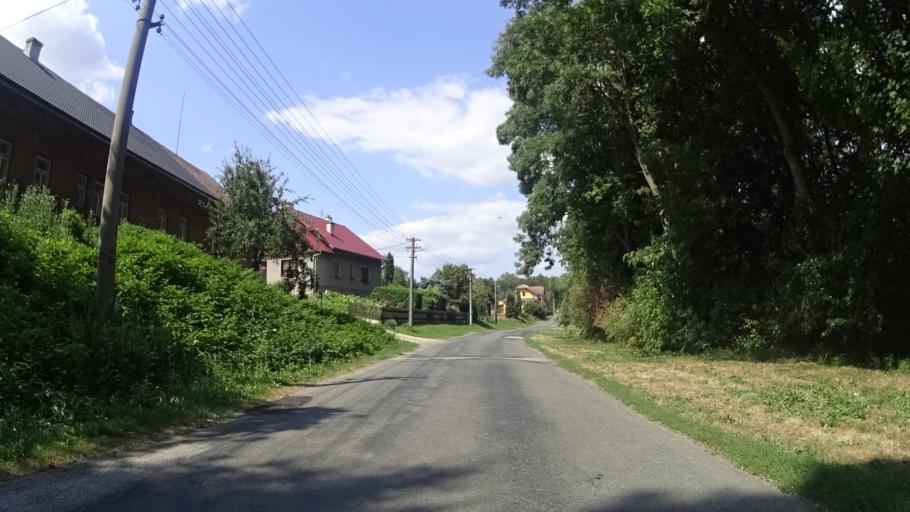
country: CZ
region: Kralovehradecky
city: Kopidlno
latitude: 50.3913
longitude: 15.2889
